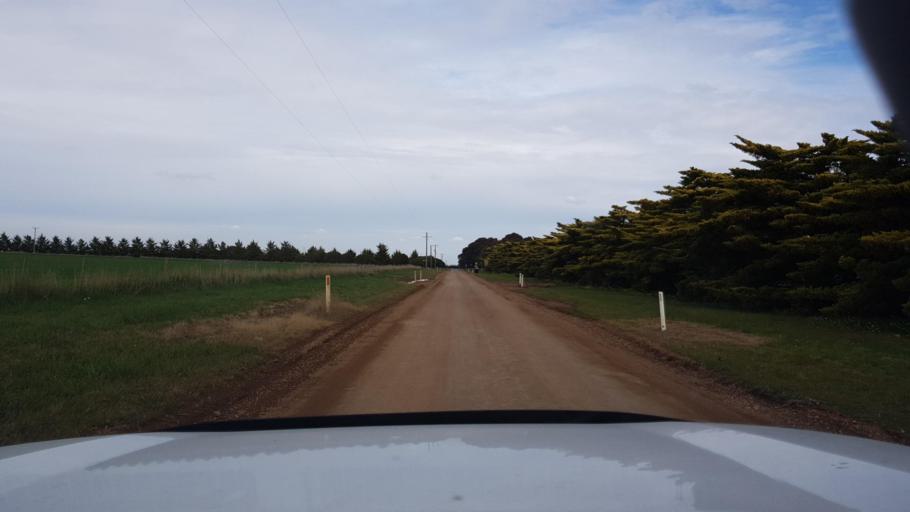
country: AU
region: Victoria
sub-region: Melton
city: Kurunjang
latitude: -37.5788
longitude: 144.6241
